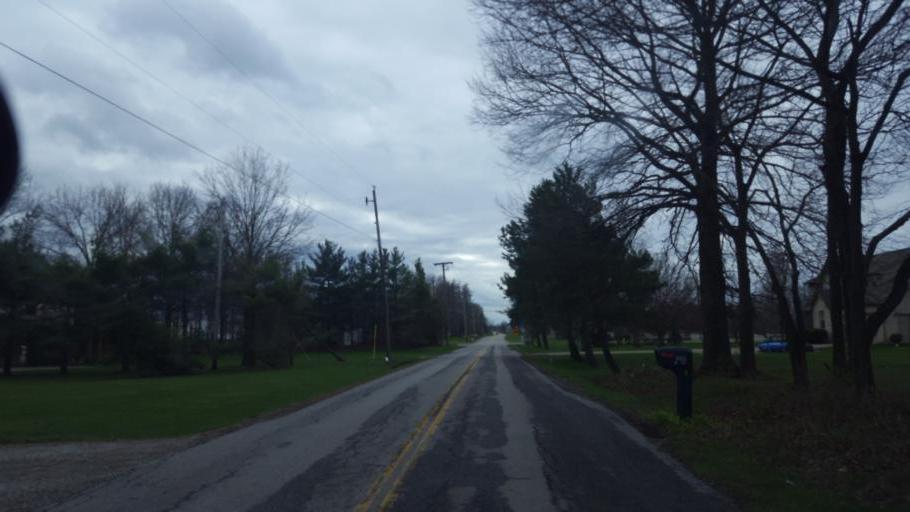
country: US
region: Ohio
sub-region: Franklin County
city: Westerville
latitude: 40.1803
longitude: -82.8991
